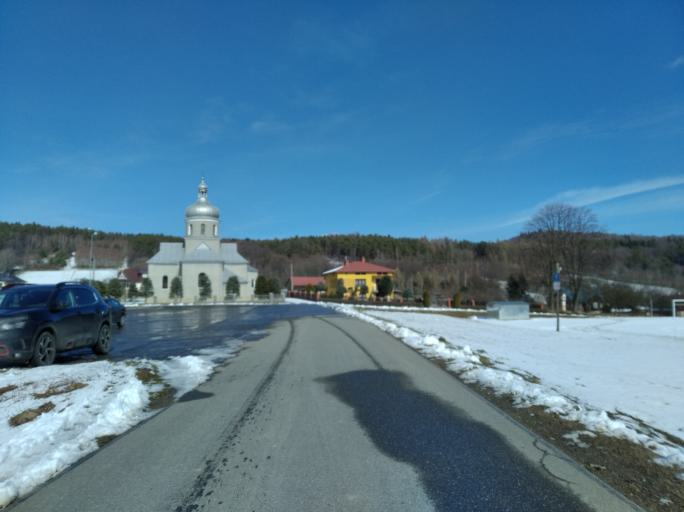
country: PL
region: Subcarpathian Voivodeship
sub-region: Powiat krosnienski
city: Korczyna
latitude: 49.7464
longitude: 21.8191
